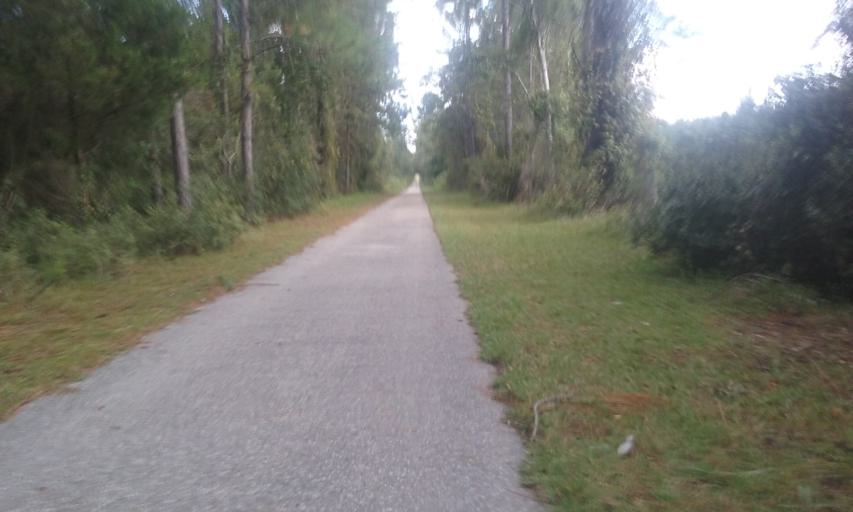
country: US
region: Florida
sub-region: Alachua County
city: Hawthorne
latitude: 29.5877
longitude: -82.1083
